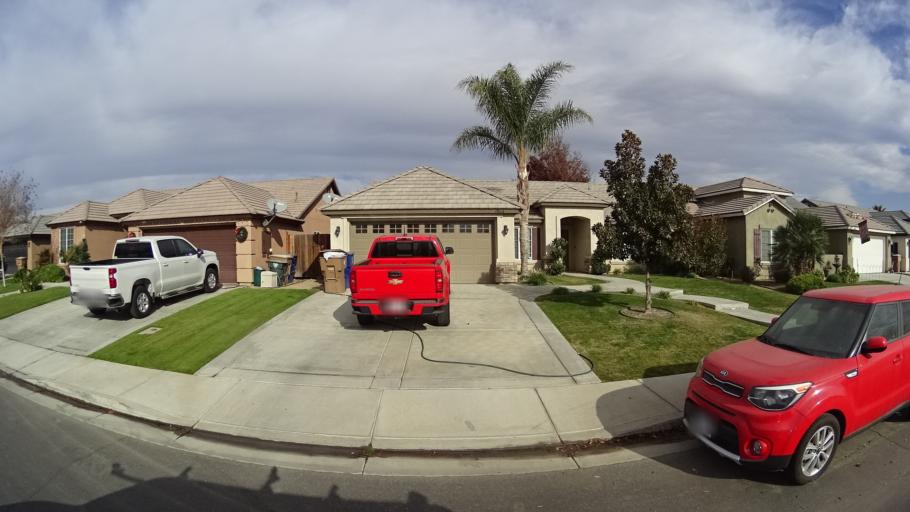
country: US
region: California
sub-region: Kern County
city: Rosedale
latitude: 35.4168
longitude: -119.1534
